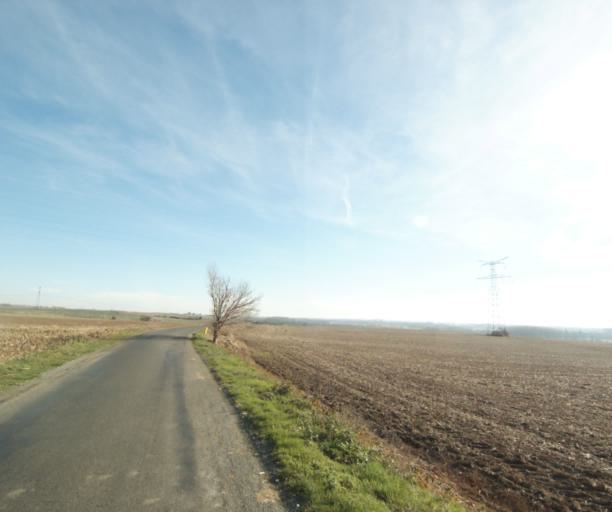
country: FR
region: Poitou-Charentes
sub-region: Departement de la Charente-Maritime
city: Les Gonds
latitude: 45.7335
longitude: -0.5946
